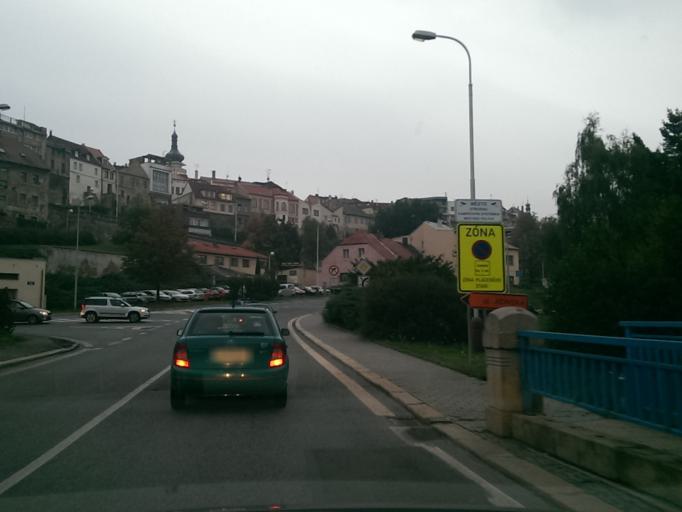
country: CZ
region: Central Bohemia
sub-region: Okres Mlada Boleslav
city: Mlada Boleslav
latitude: 50.4089
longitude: 14.9034
